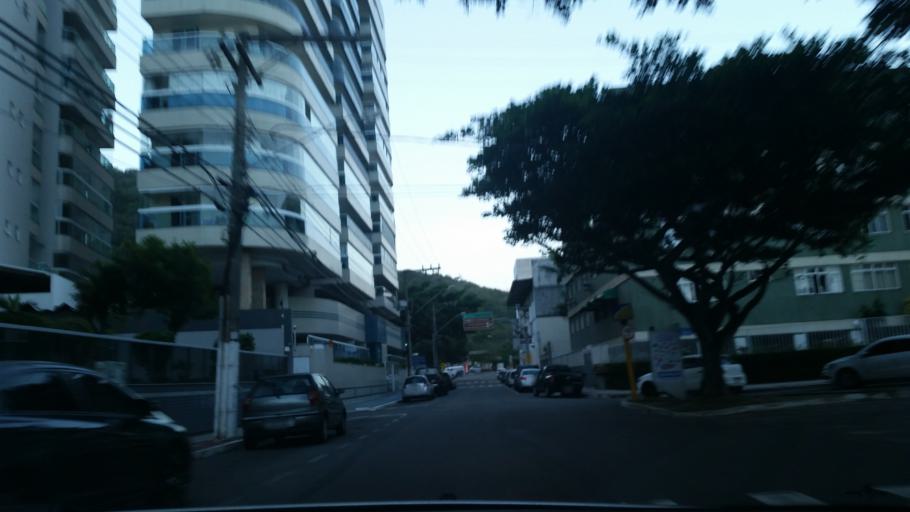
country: BR
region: Espirito Santo
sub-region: Vila Velha
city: Vila Velha
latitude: -20.3291
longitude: -40.2735
